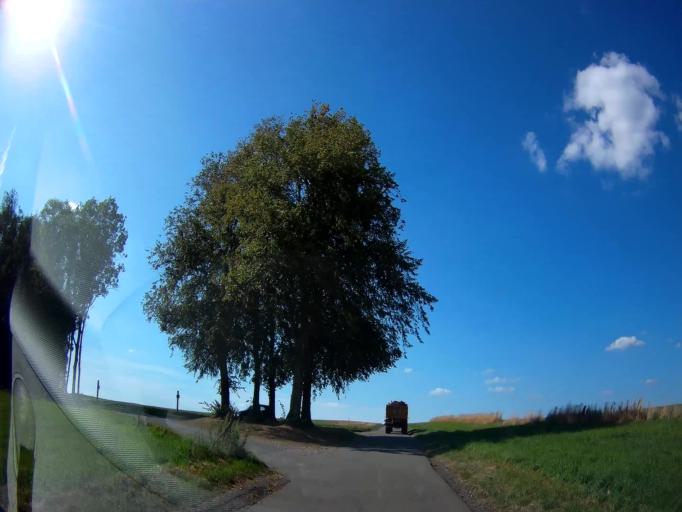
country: BE
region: Wallonia
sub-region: Province de Namur
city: Dinant
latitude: 50.2362
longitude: 4.9690
